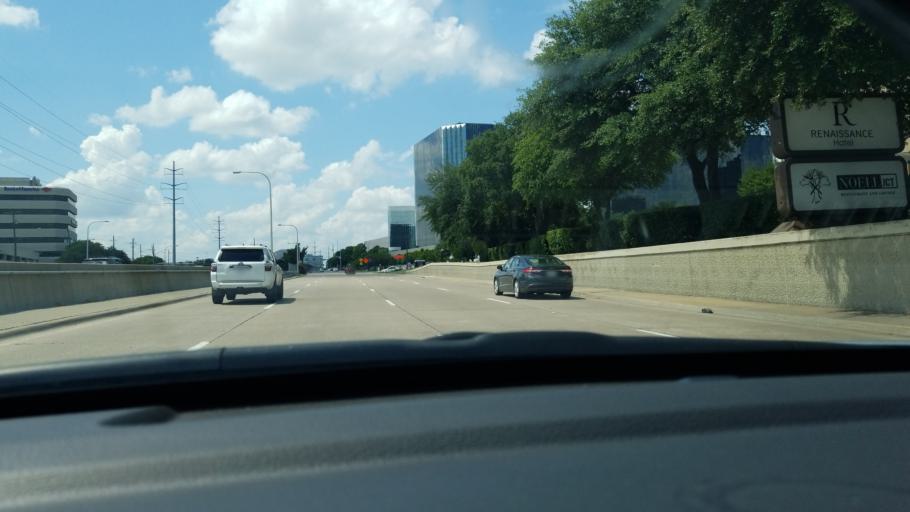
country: US
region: Texas
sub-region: Dallas County
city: Addison
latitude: 32.9569
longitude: -96.8218
